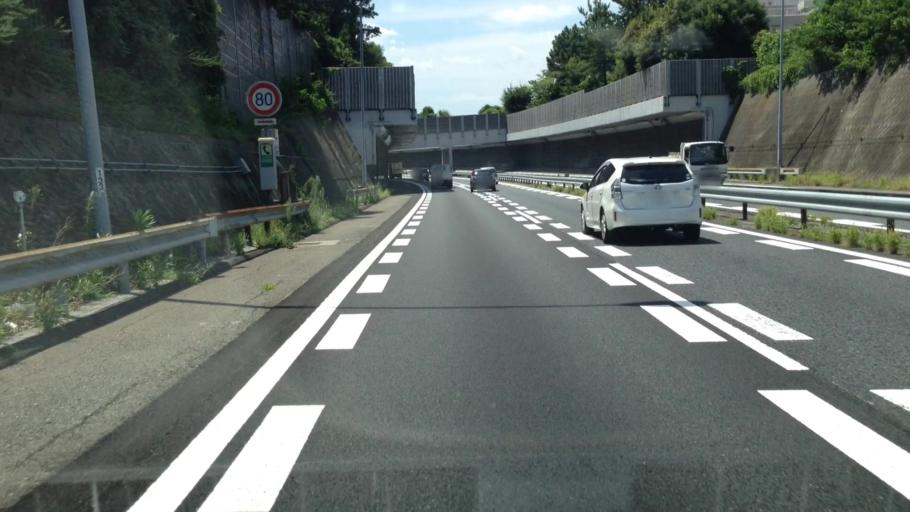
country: JP
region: Kanagawa
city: Yokohama
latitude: 35.4119
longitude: 139.5778
